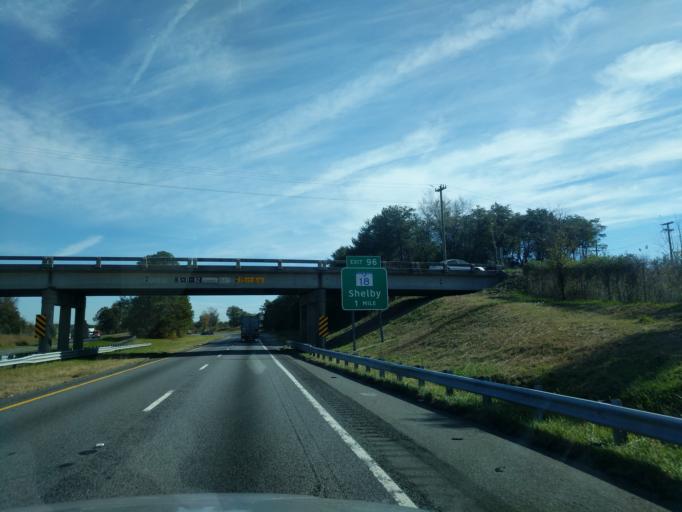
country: US
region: South Carolina
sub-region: Cherokee County
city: East Gaffney
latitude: 35.1026
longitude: -81.6271
